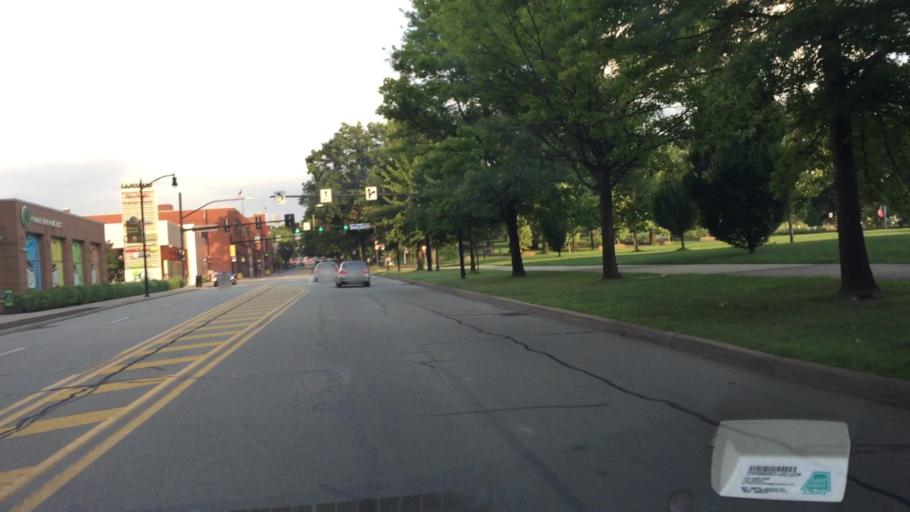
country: US
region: Pennsylvania
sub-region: Allegheny County
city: Bloomfield
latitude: 40.4567
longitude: -79.9164
